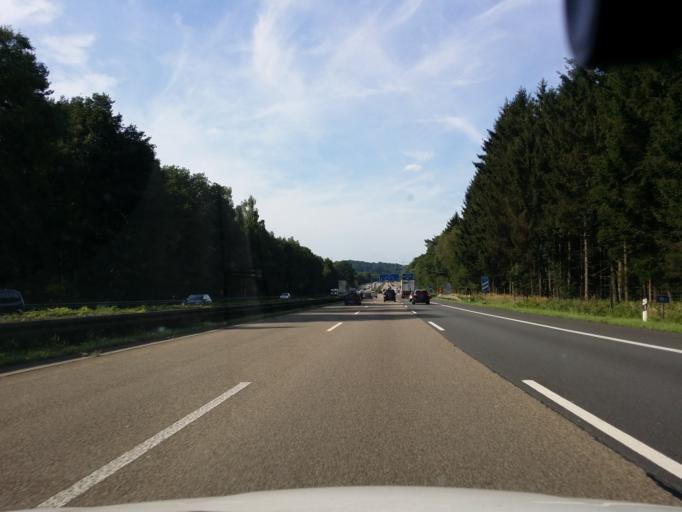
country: DE
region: North Rhine-Westphalia
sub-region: Regierungsbezirk Koln
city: Siegburg
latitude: 50.8176
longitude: 7.2105
